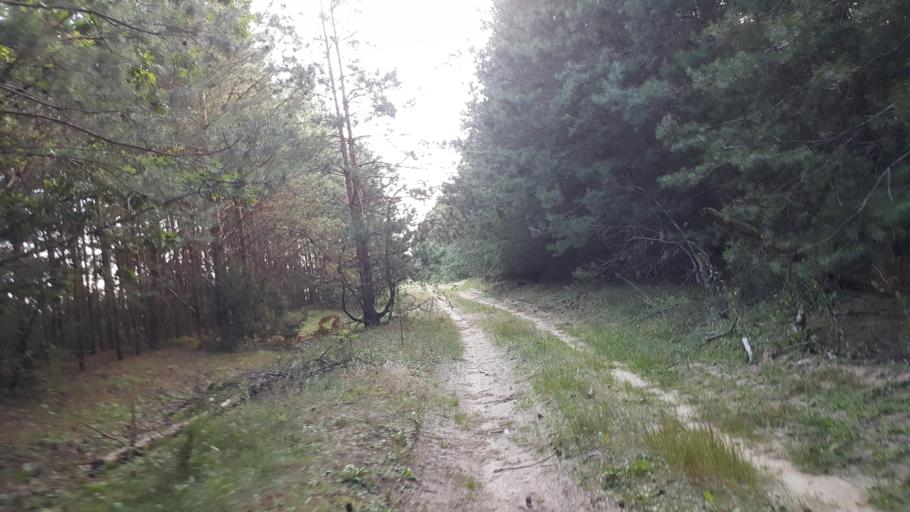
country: BY
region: Brest
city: Zhabinka
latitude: 52.3645
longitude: 24.1571
